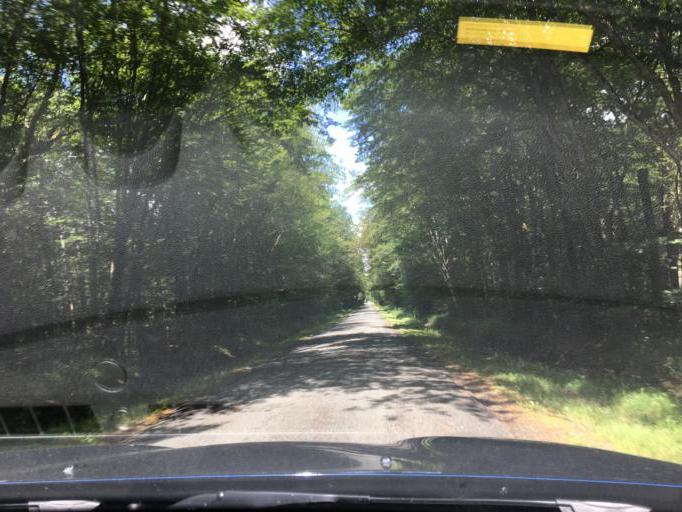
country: FR
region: Centre
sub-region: Departement du Loiret
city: Chanteau
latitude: 48.0020
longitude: 1.9351
